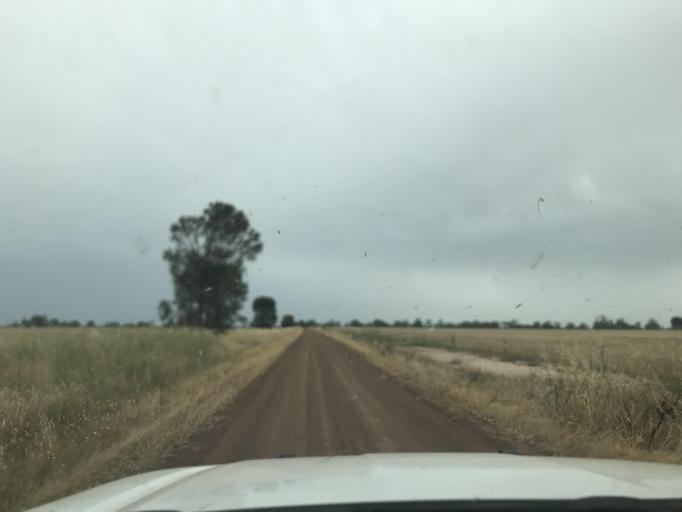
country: AU
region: Victoria
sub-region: Horsham
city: Horsham
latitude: -37.0638
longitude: 141.6439
